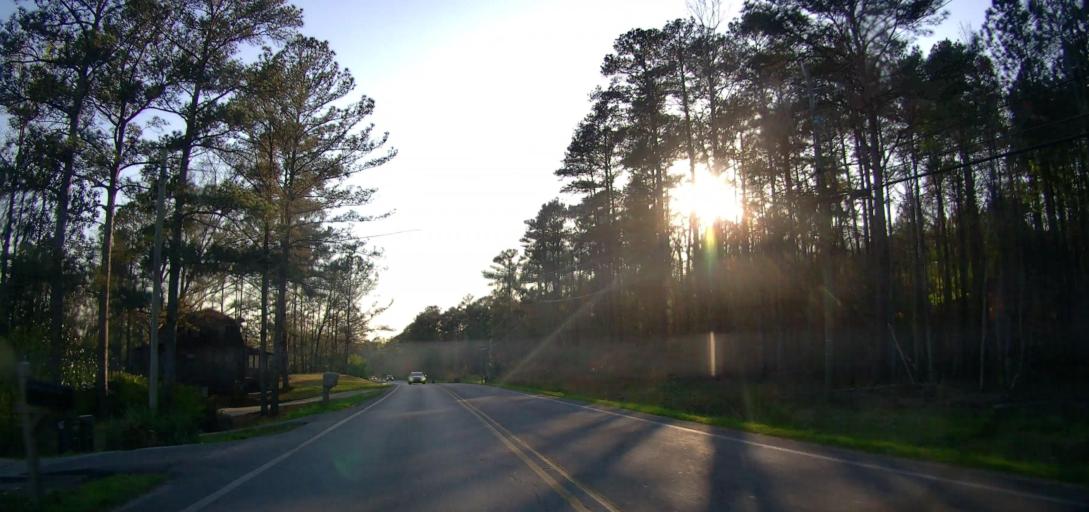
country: US
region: Alabama
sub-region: Shelby County
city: Pelham
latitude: 33.2823
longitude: -86.7747
